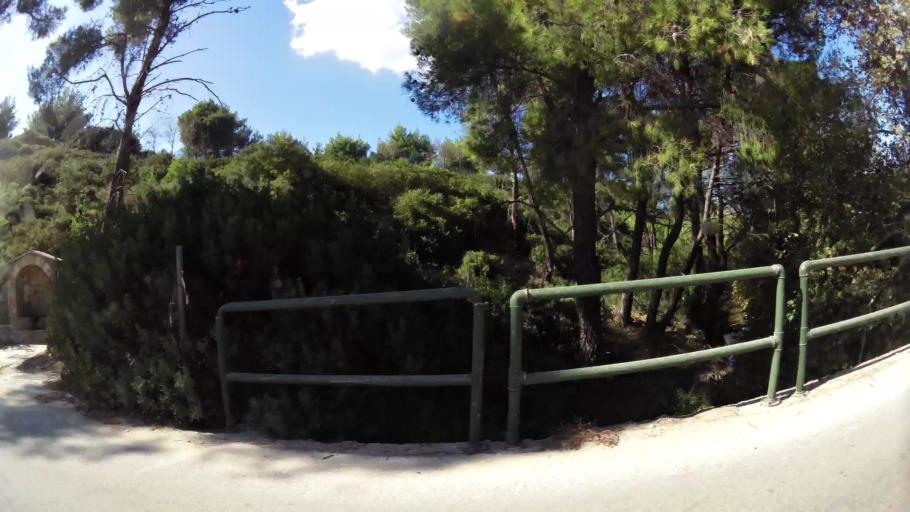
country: GR
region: Attica
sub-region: Nomarchia Anatolikis Attikis
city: Dioni
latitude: 38.0137
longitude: 23.9329
